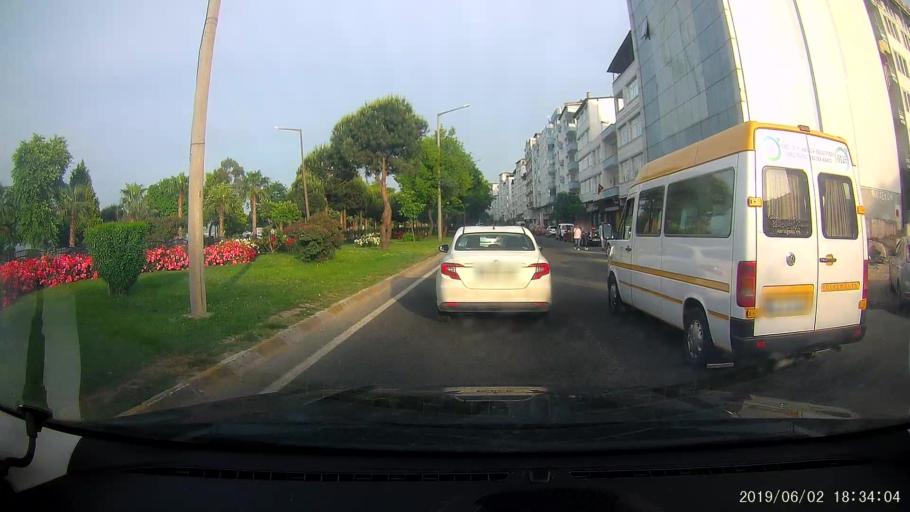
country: TR
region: Ordu
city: Fatsa
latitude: 41.0314
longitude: 37.5007
